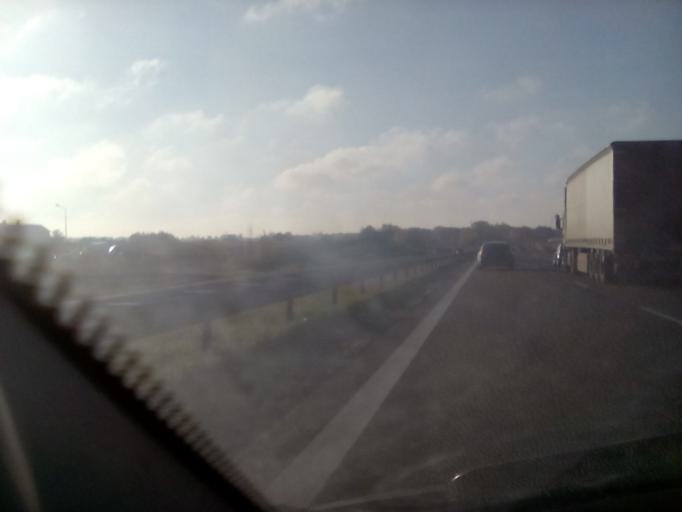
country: PL
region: Masovian Voivodeship
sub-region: Powiat grojecki
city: Grojec
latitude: 51.8842
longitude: 20.8559
